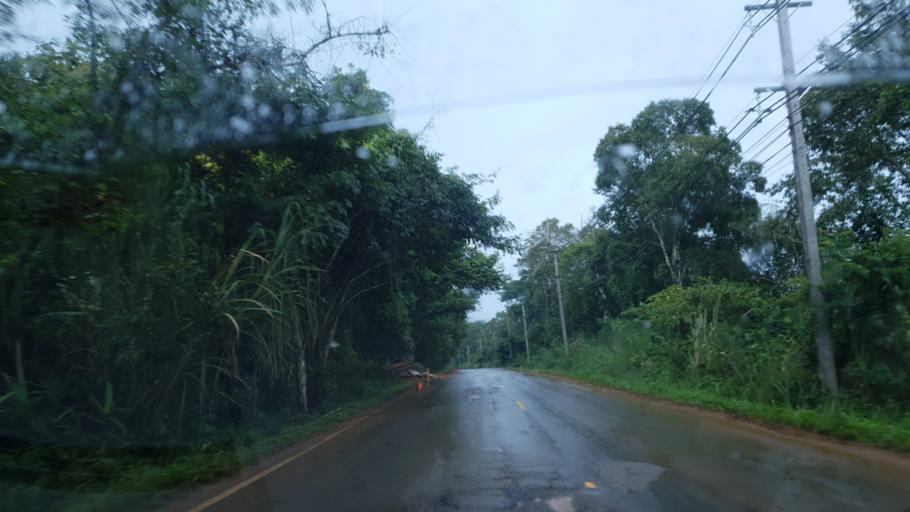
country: TH
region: Mae Hong Son
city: Ban Huai I Huak
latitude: 18.1418
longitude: 98.0744
